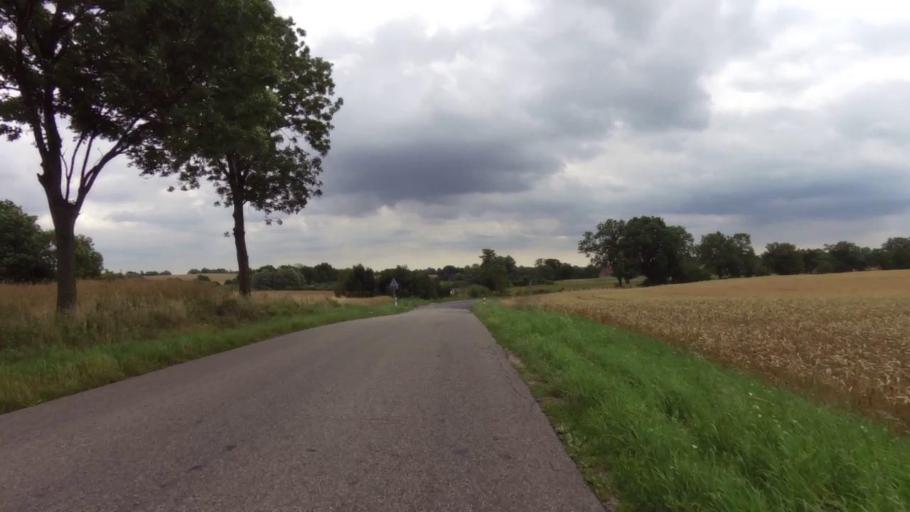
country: PL
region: West Pomeranian Voivodeship
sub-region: Powiat gryfinski
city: Cedynia
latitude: 52.8662
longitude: 14.2577
